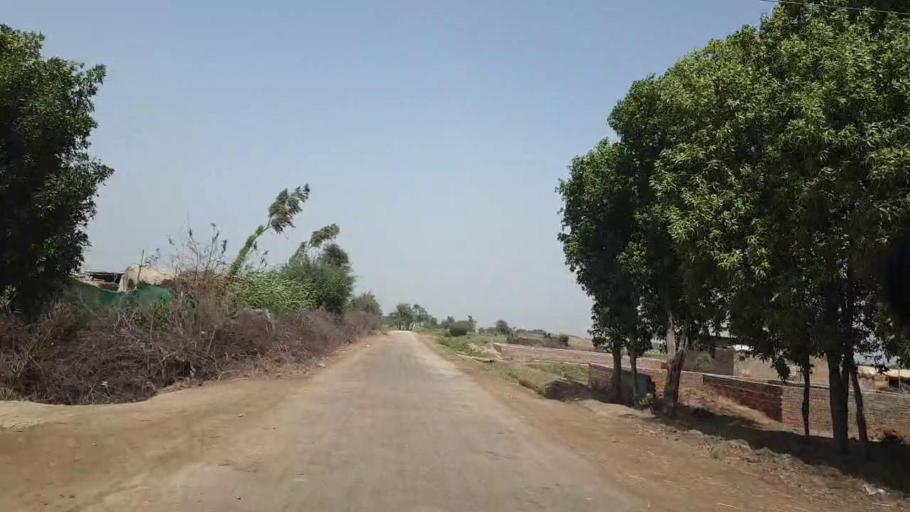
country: PK
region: Sindh
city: Matli
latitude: 25.0560
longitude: 68.6927
